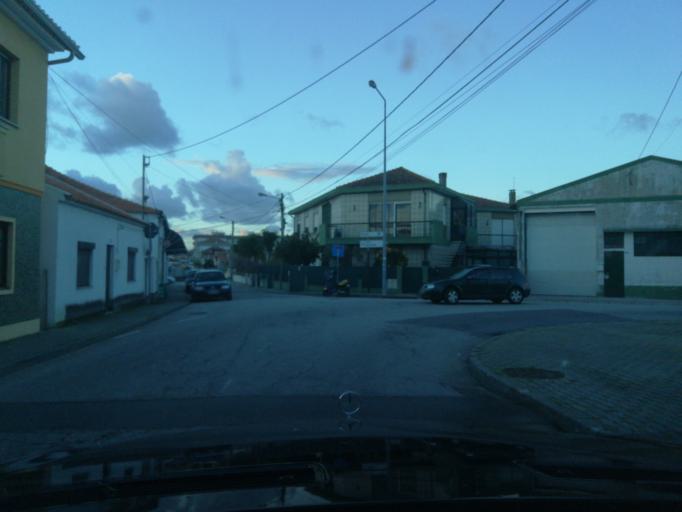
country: PT
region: Aveiro
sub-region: Estarreja
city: Estarreja
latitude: 40.7572
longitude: -8.5759
